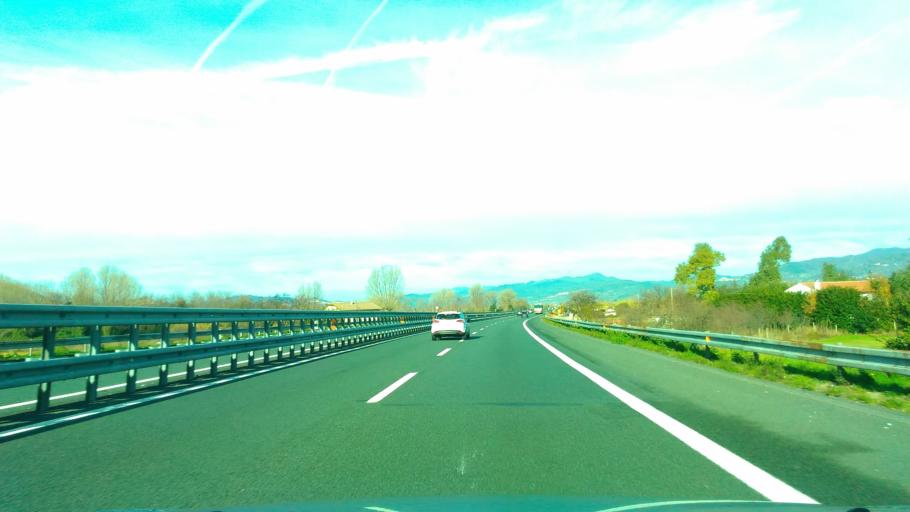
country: IT
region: Liguria
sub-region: Provincia di La Spezia
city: Ameglia
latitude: 44.0787
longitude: 9.9797
